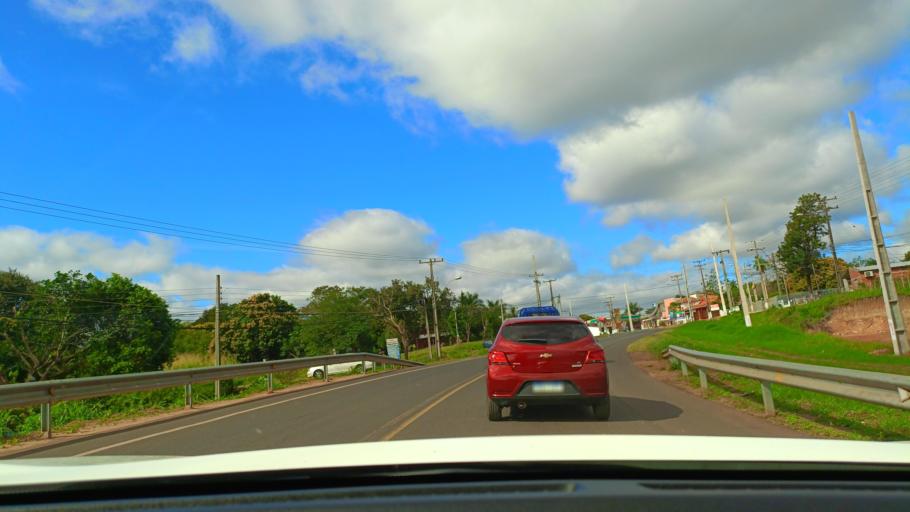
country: PY
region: San Pedro
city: Guayaybi
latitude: -24.6634
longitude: -56.4316
